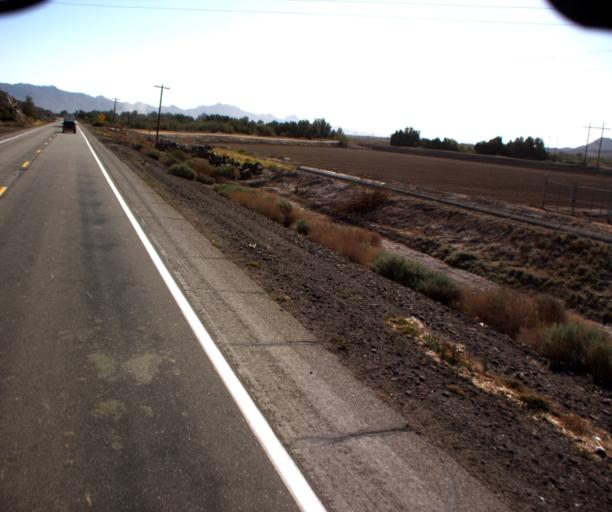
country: US
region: Arizona
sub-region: Yuma County
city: Fortuna Foothills
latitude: 32.7690
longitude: -114.3971
